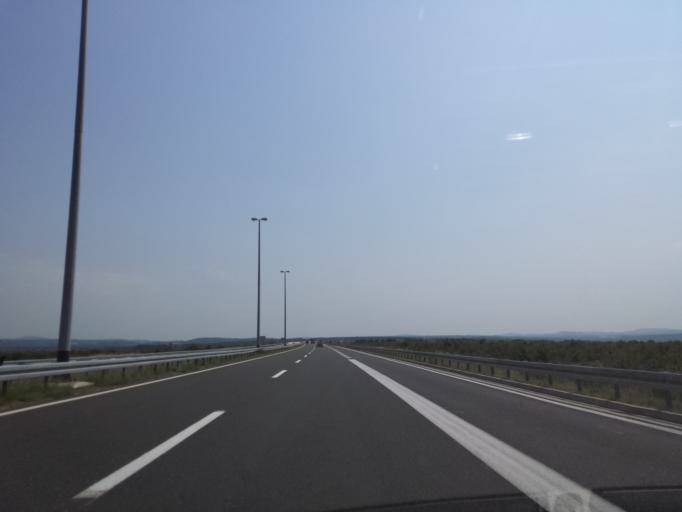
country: HR
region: Zadarska
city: Polaca
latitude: 44.0603
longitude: 15.5329
